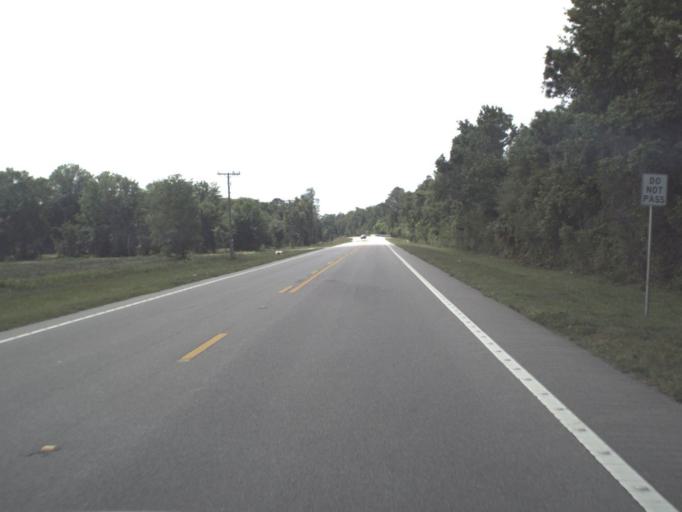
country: US
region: Florida
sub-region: Flagler County
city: Bunnell
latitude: 29.4795
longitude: -81.3408
